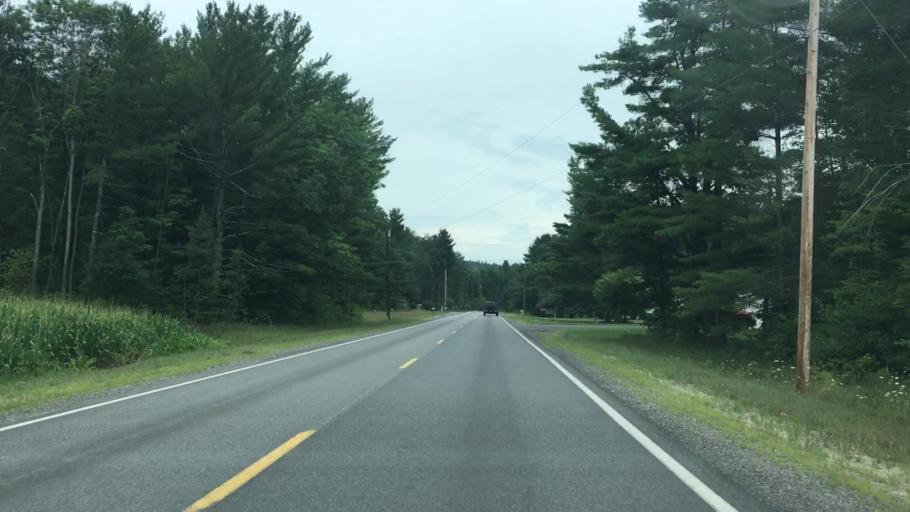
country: US
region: New York
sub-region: Clinton County
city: Peru
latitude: 44.5104
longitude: -73.5828
